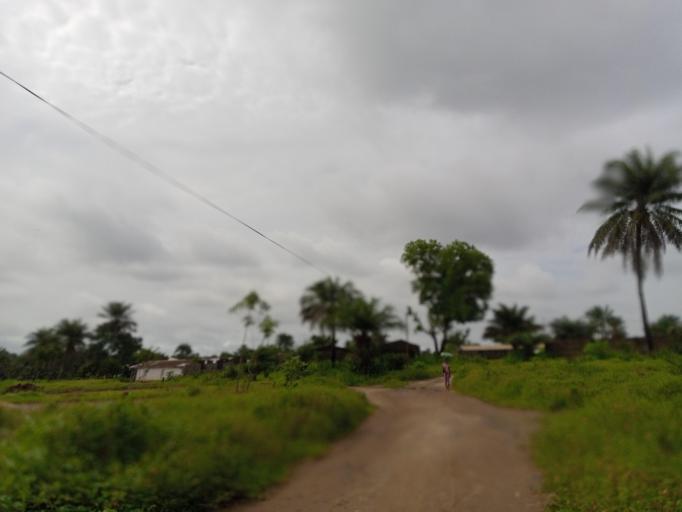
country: SL
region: Northern Province
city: Sawkta
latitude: 8.6256
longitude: -13.1978
